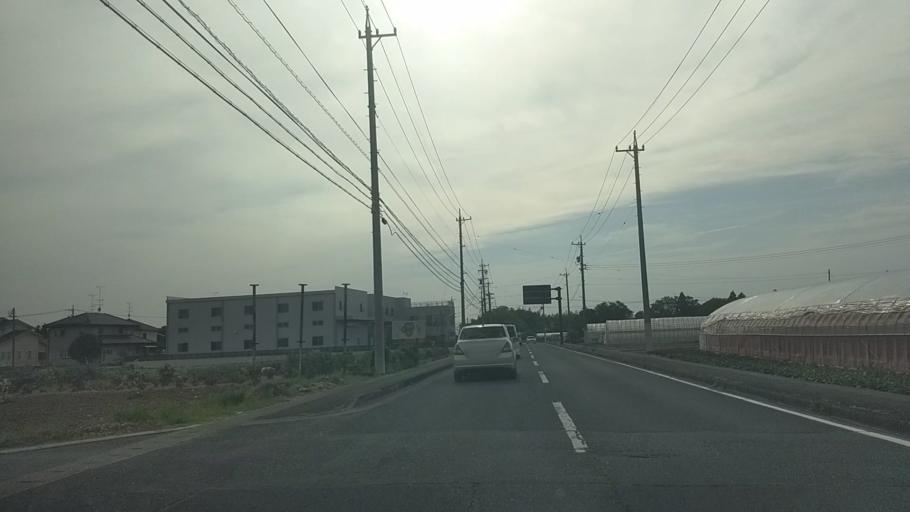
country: JP
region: Shizuoka
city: Kosai-shi
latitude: 34.7603
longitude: 137.6247
